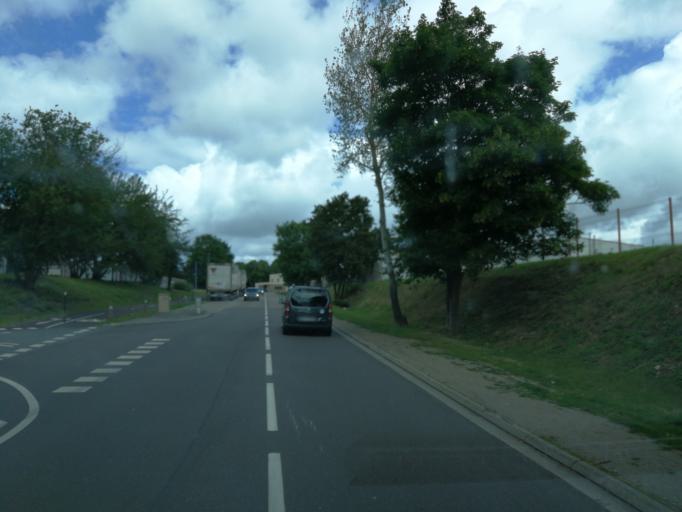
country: FR
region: Haute-Normandie
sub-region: Departement de l'Eure
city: Le Vaudreuil
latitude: 49.2500
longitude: 1.1820
